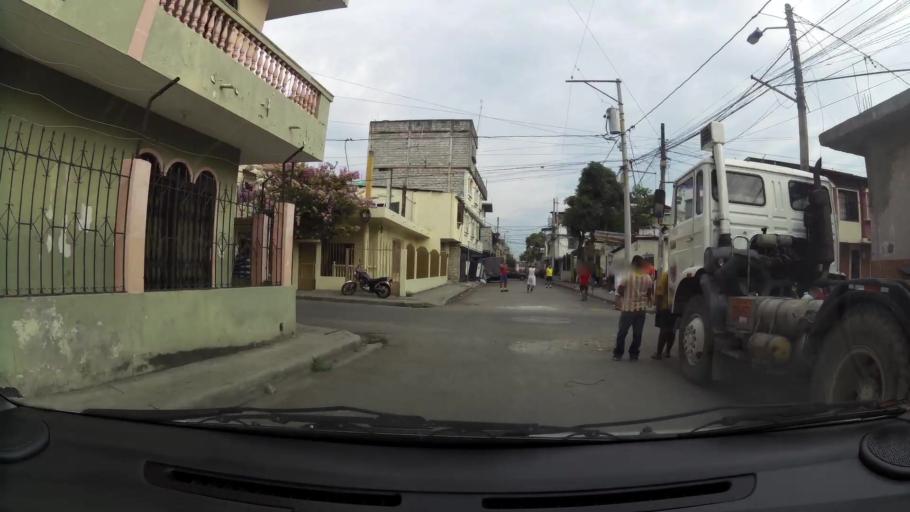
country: EC
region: Guayas
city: Guayaquil
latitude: -2.2527
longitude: -79.8956
